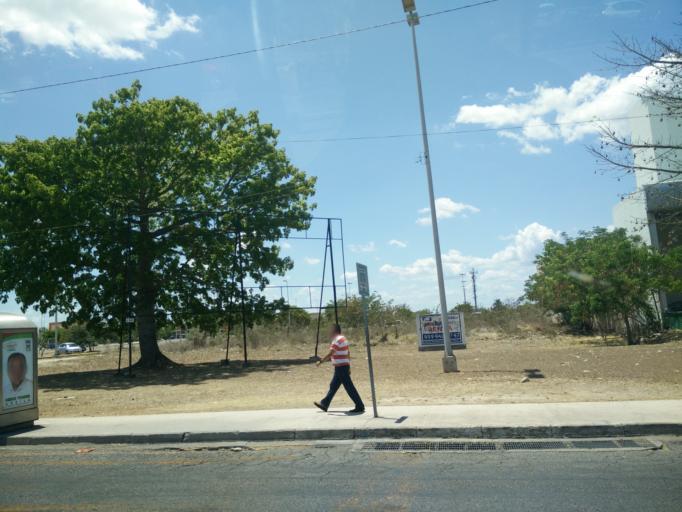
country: MX
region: Yucatan
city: Merida
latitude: 21.0320
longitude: -89.6274
